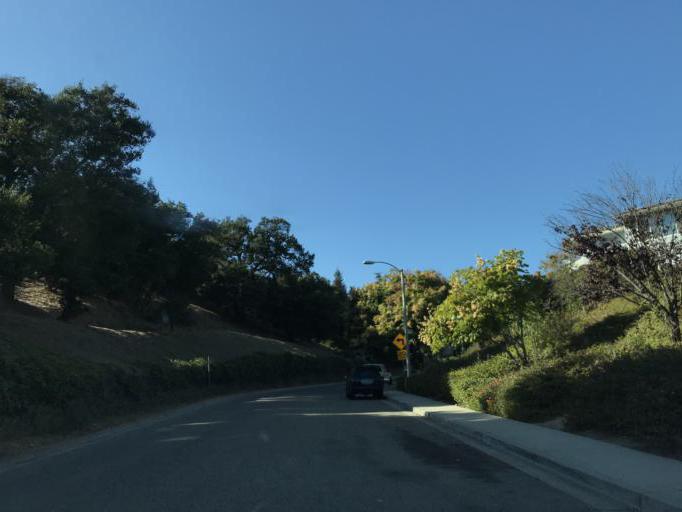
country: US
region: California
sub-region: Santa Barbara County
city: Goleta
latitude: 34.4478
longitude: -119.7799
